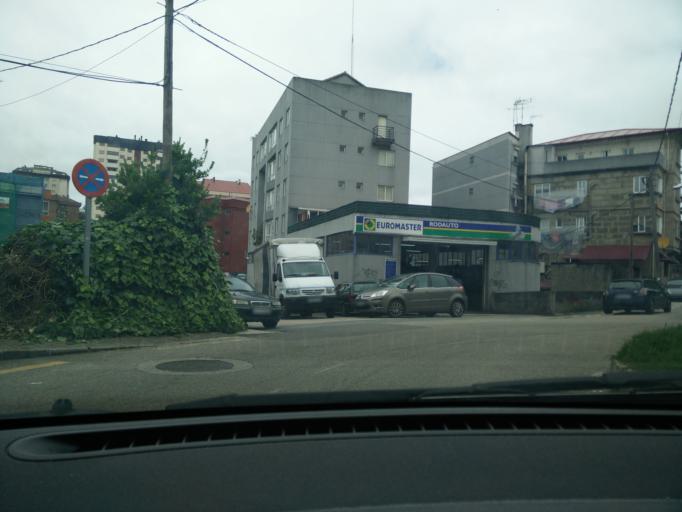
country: ES
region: Galicia
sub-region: Provincia de Pontevedra
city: Vigo
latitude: 42.2127
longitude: -8.7434
